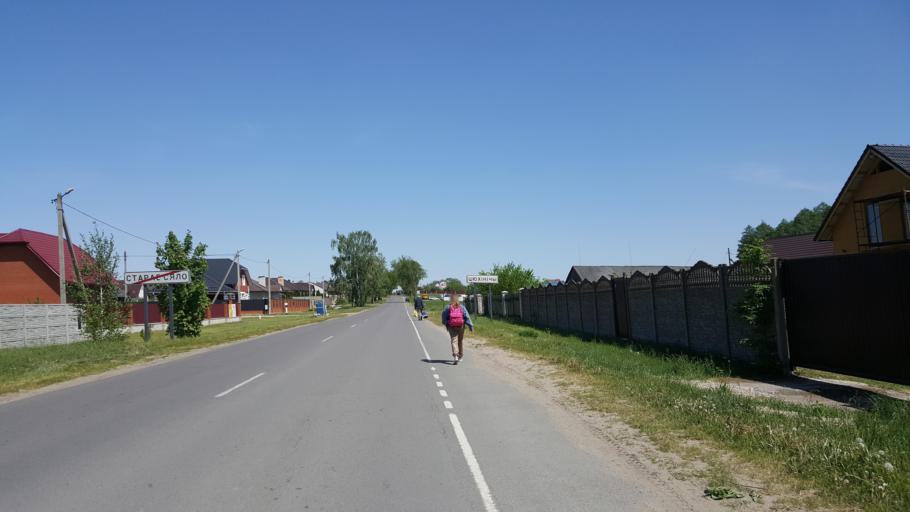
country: BY
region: Brest
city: Brest
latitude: 52.1593
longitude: 23.6550
